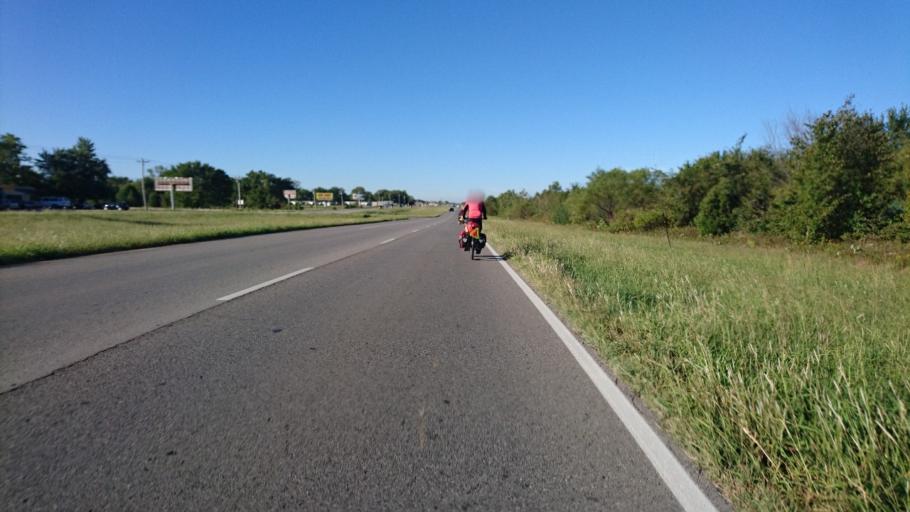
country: US
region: Oklahoma
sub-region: Rogers County
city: Verdigris
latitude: 36.2678
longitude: -95.6491
